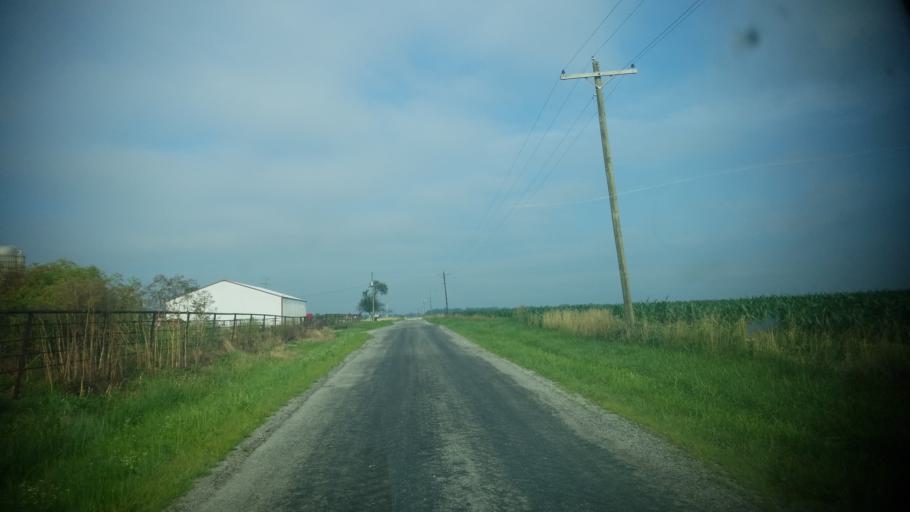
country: US
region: Illinois
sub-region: Clay County
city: Flora
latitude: 38.6015
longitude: -88.3395
